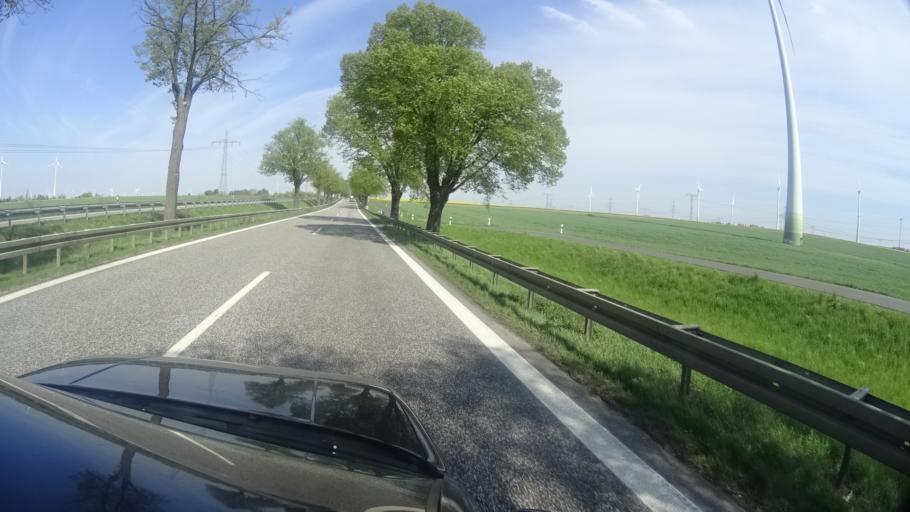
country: DE
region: Brandenburg
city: Wustermark
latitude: 52.5666
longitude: 12.9197
